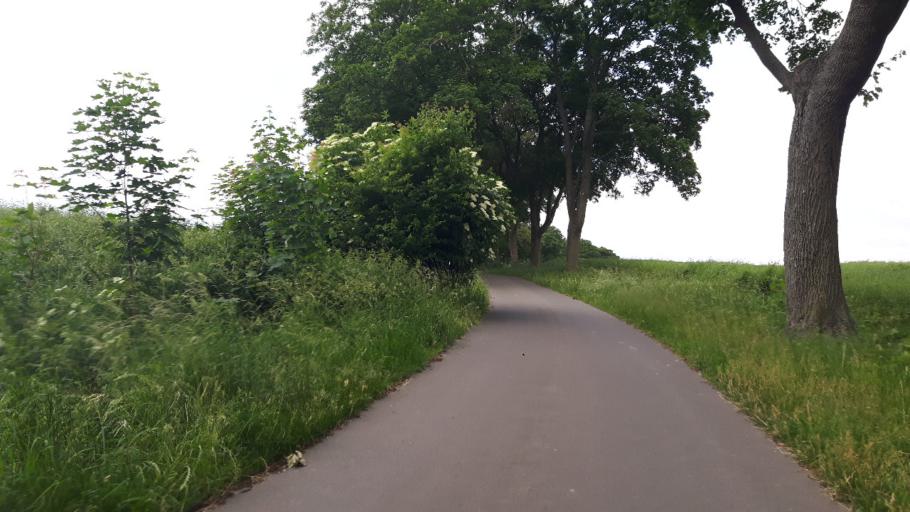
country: DE
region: Brandenburg
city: Mescherin
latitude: 53.2757
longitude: 14.4224
